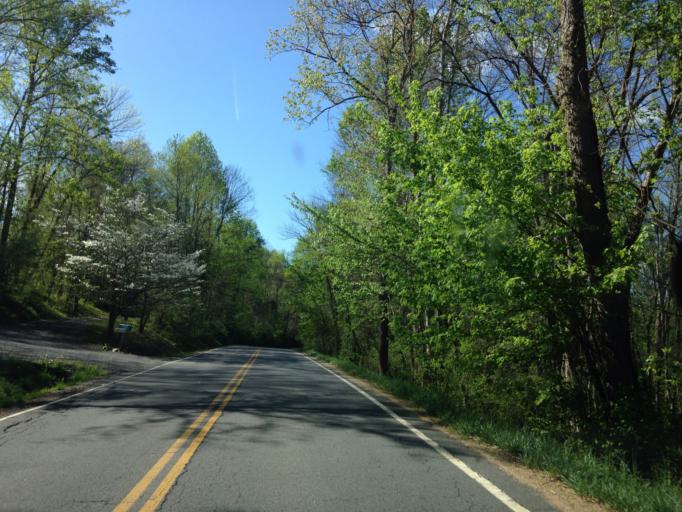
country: US
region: Maryland
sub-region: Frederick County
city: Point of Rocks
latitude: 39.2743
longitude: -77.5522
